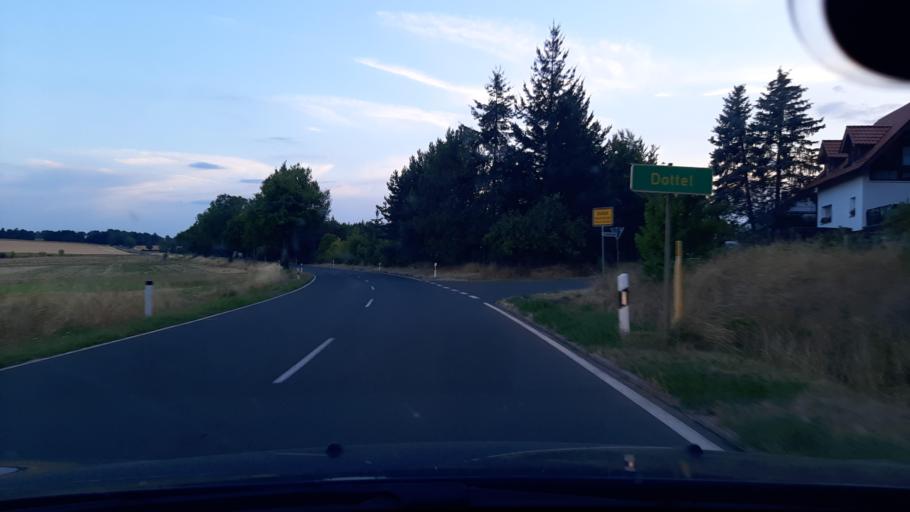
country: DE
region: North Rhine-Westphalia
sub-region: Regierungsbezirk Koln
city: Kall
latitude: 50.5496
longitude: 6.6009
